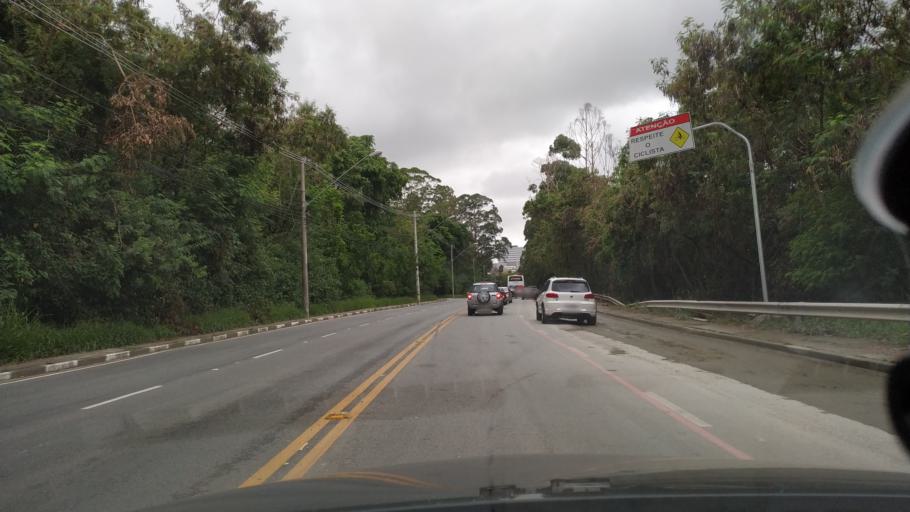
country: BR
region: Sao Paulo
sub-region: Barueri
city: Barueri
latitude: -23.4932
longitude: -46.8657
